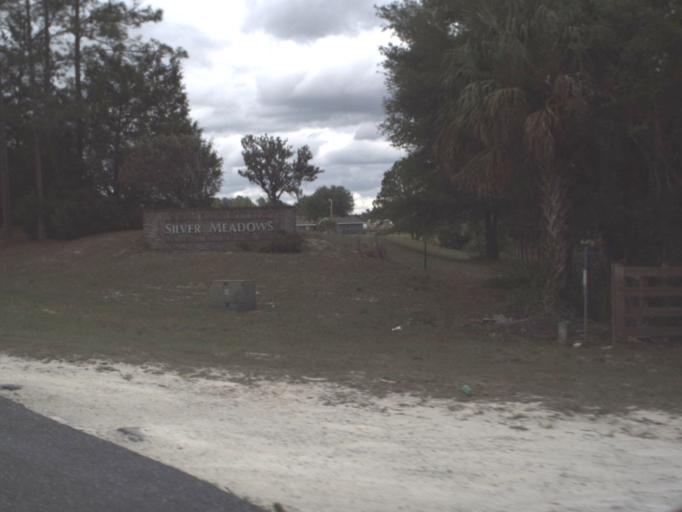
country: US
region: Florida
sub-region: Marion County
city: Ocala
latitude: 29.2328
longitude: -82.0439
